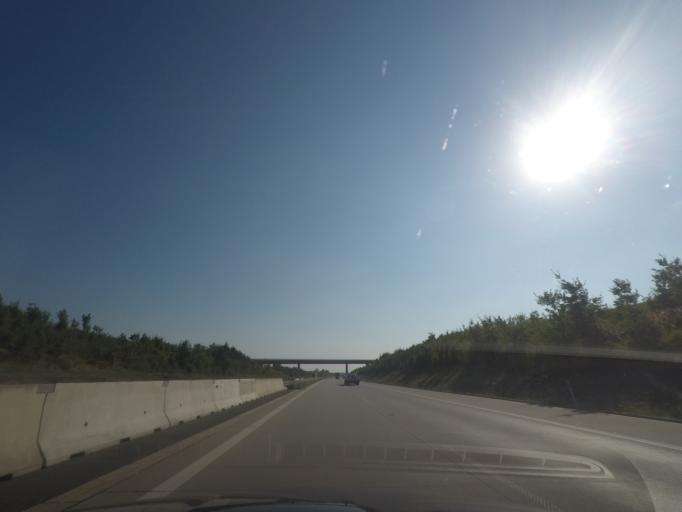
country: CZ
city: Bilovec
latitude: 49.7063
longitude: 17.9916
